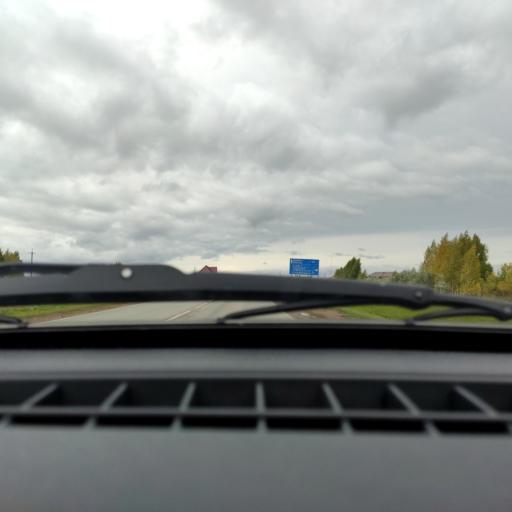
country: RU
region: Bashkortostan
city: Rayevskiy
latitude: 54.0752
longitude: 54.9120
